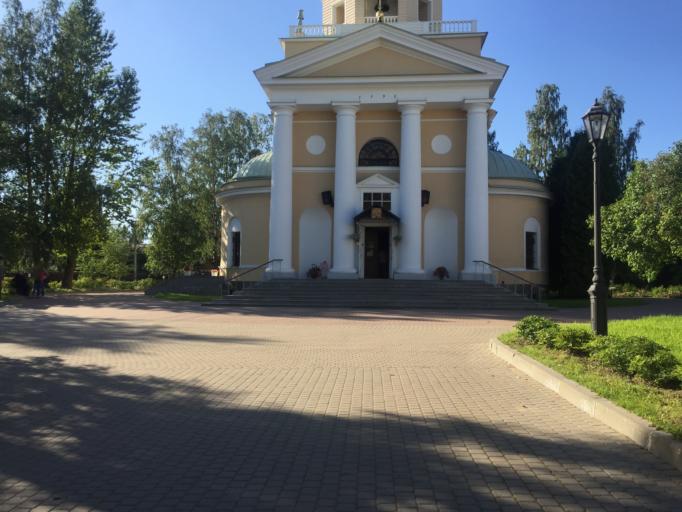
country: RU
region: Leningrad
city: Murino
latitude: 60.0434
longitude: 30.4438
